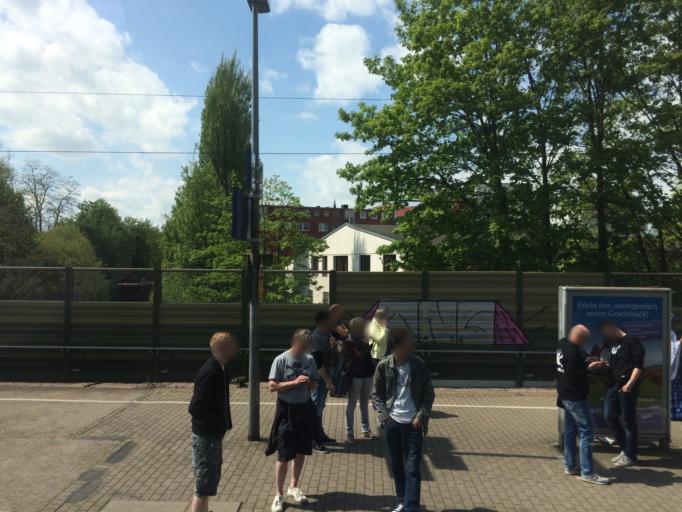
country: DE
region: Schleswig-Holstein
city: Elmshorn
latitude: 53.7541
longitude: 9.6595
